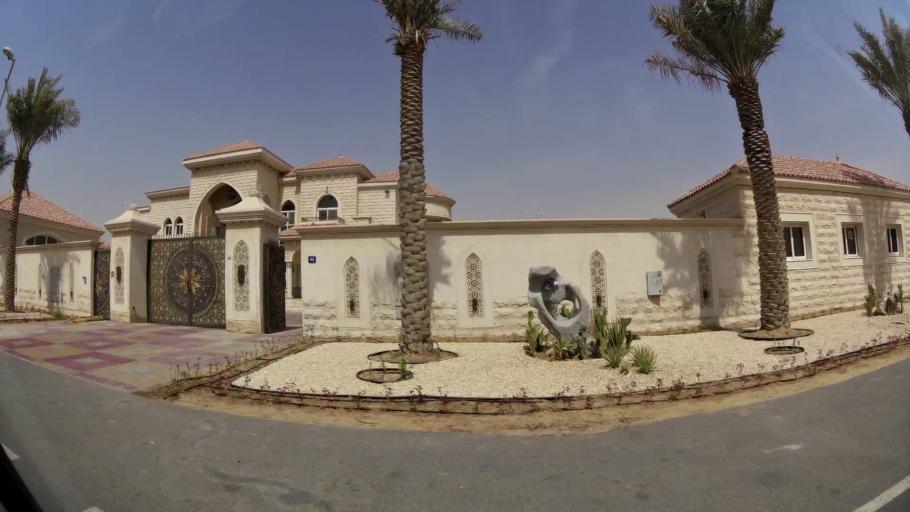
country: AE
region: Ash Shariqah
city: Sharjah
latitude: 25.2519
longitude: 55.4846
